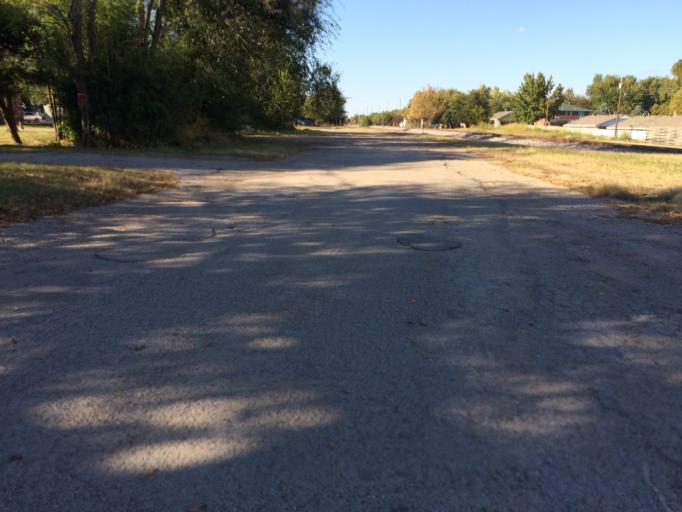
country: US
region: Oklahoma
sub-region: Cleveland County
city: Norman
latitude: 35.2113
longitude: -97.4378
